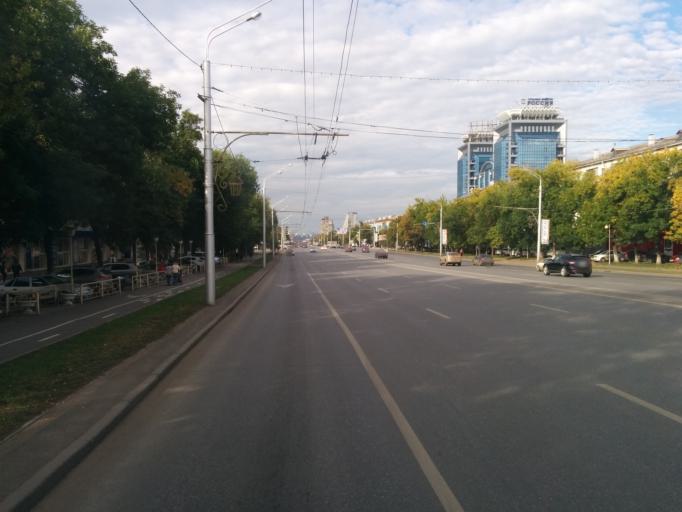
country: RU
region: Bashkortostan
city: Ufa
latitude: 54.7751
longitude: 56.0290
